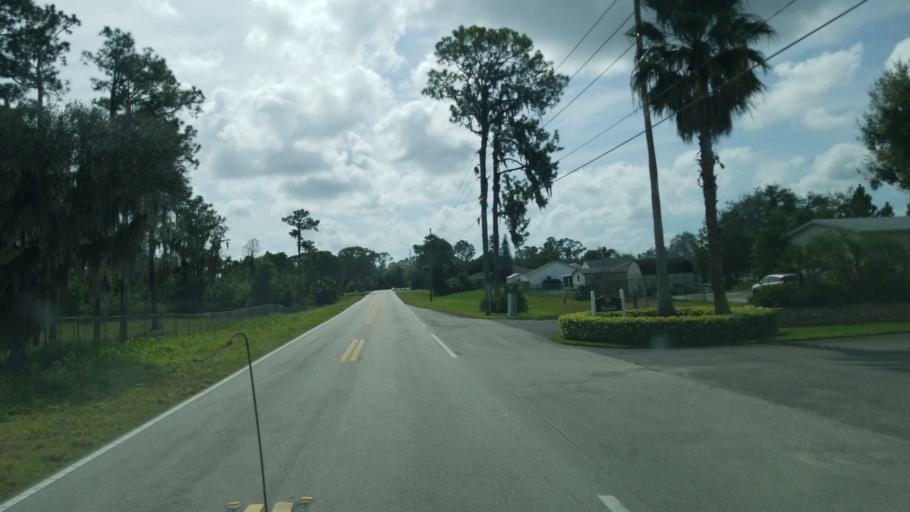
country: US
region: Florida
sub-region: Polk County
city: Dundee
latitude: 28.0008
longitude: -81.5255
